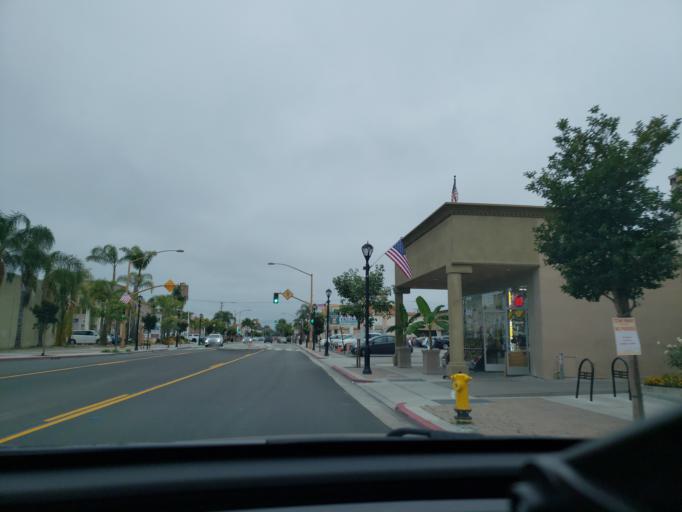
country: US
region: California
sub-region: Los Angeles County
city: Artesia
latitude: 33.8646
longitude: -118.0823
